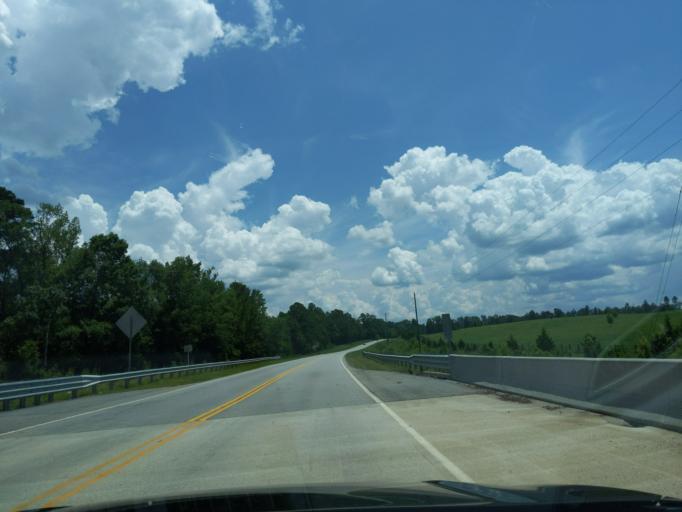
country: US
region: South Carolina
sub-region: Edgefield County
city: Edgefield
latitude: 33.8635
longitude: -81.9868
